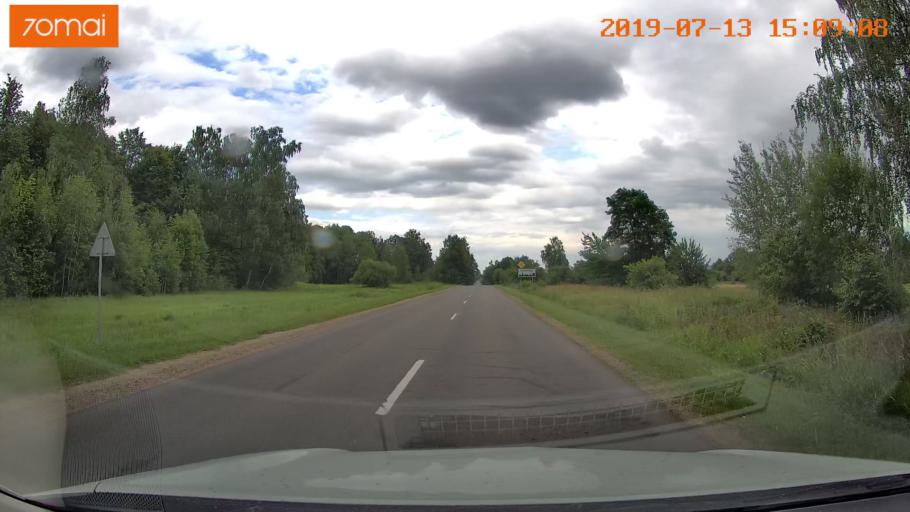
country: BY
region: Mogilev
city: Hlusha
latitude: 53.1740
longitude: 28.7572
